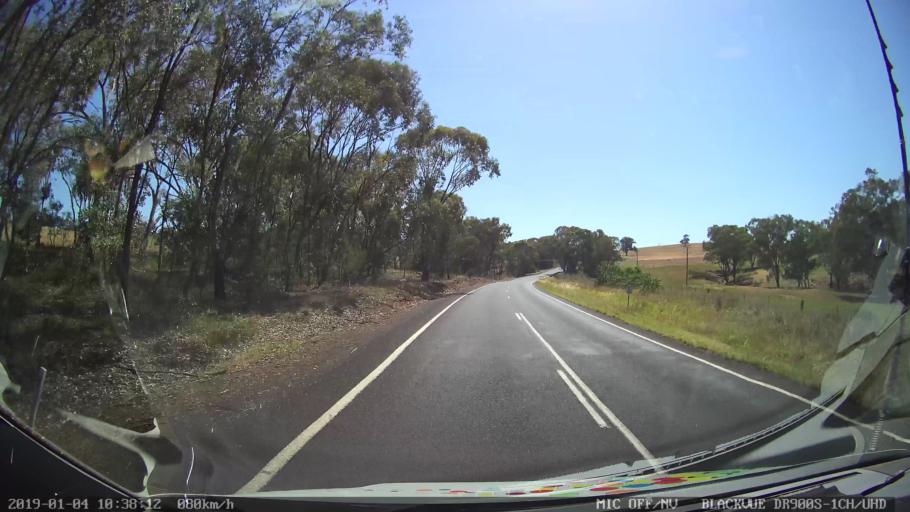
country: AU
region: New South Wales
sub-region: Cabonne
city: Molong
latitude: -33.2937
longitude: 148.7054
